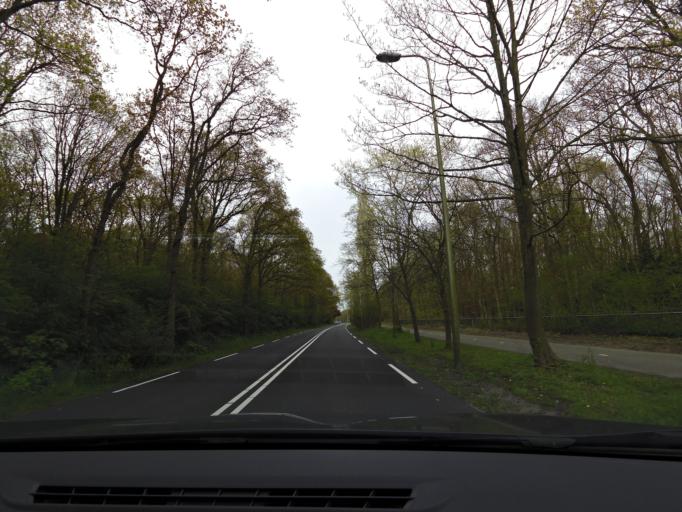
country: NL
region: South Holland
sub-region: Gemeente Noordwijk
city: Noordwijk-Binnen
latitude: 52.2449
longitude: 4.4661
